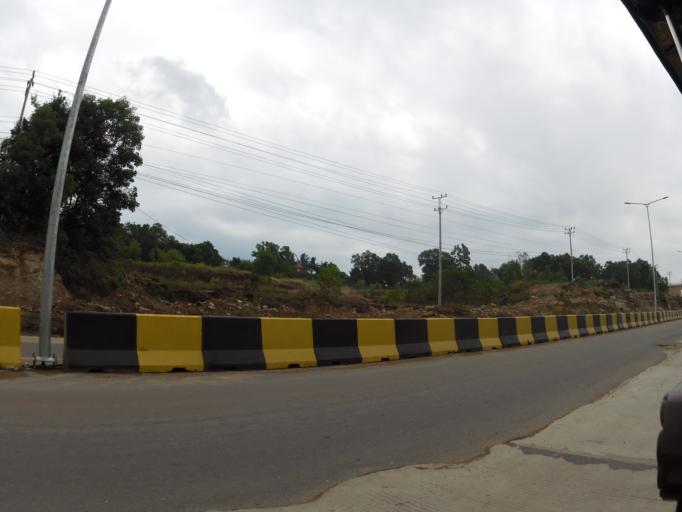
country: KH
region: Preah Sihanouk
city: Sihanoukville
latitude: 10.6406
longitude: 103.5288
